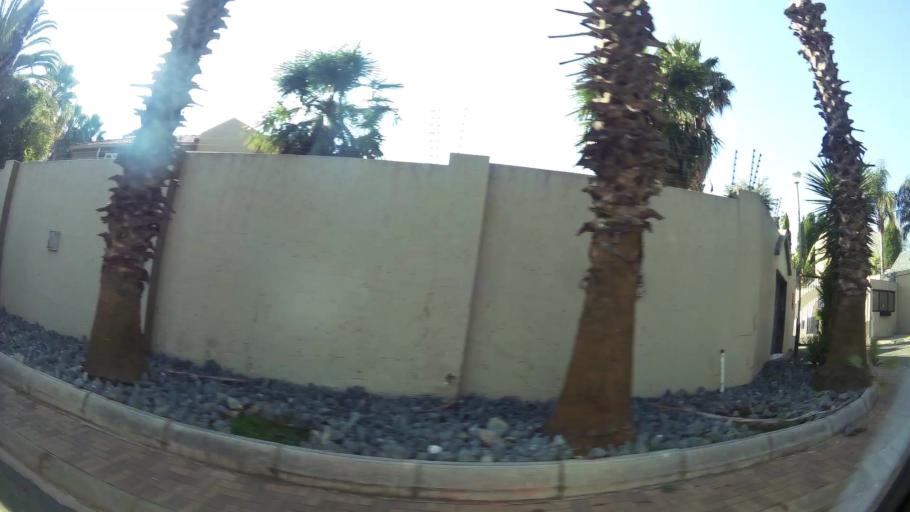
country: ZA
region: Gauteng
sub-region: Ekurhuleni Metropolitan Municipality
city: Germiston
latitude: -26.1706
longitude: 28.1533
